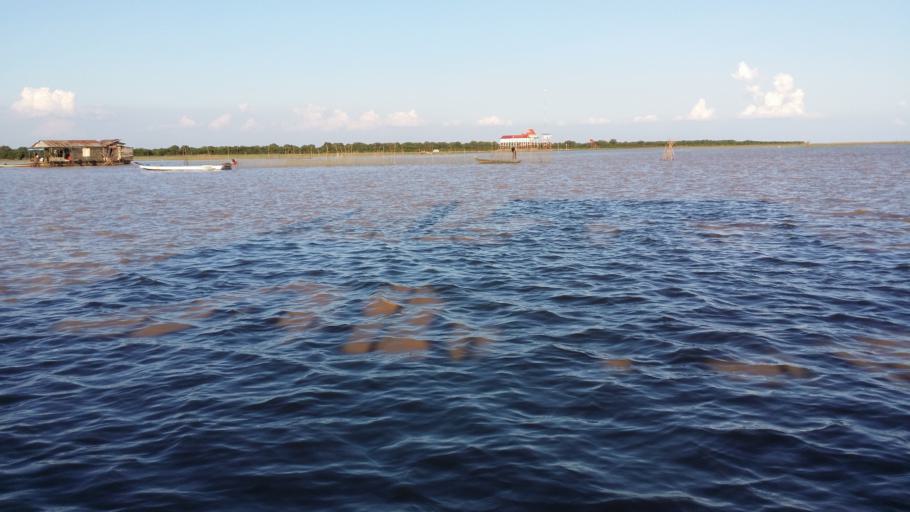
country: KH
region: Siem Reap
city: Siem Reap
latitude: 13.2306
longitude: 103.8275
